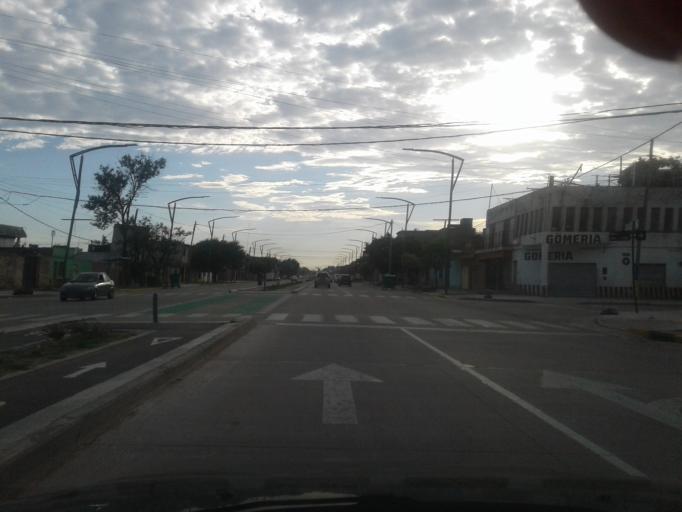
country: AR
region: Santa Fe
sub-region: Departamento de Rosario
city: Rosario
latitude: -32.9593
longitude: -60.7064
